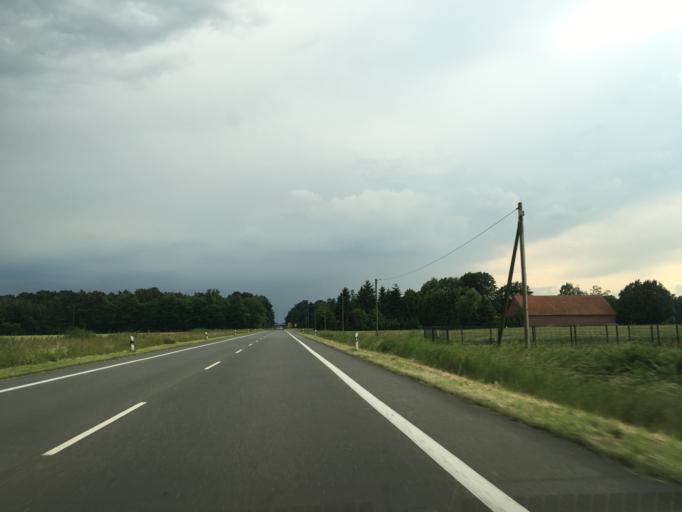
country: DE
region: North Rhine-Westphalia
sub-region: Regierungsbezirk Munster
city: Wettringen
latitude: 52.1767
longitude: 7.2698
